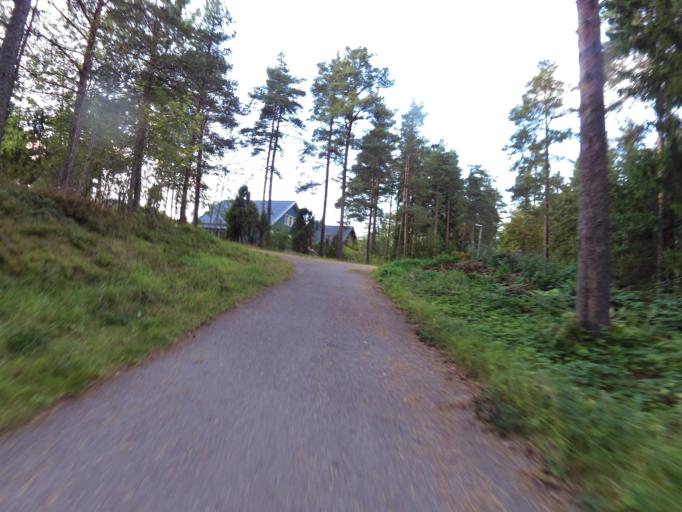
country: SE
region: Gaevleborg
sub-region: Gavle Kommun
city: Gavle
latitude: 60.6684
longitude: 17.2331
